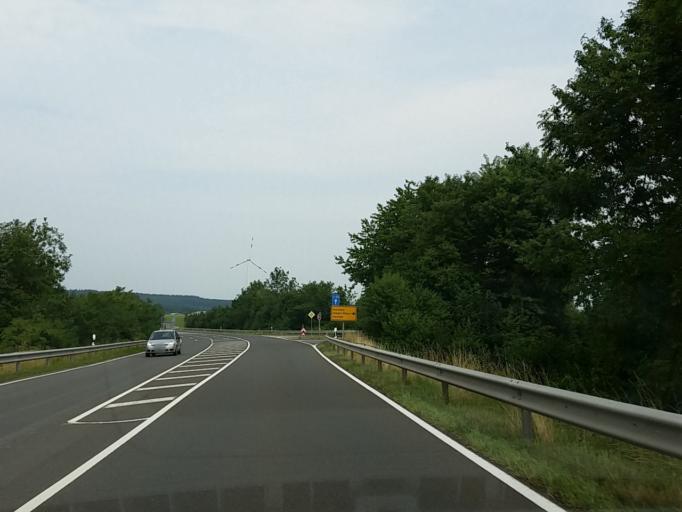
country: DE
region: Rheinland-Pfalz
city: Reinsfeld
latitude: 49.6808
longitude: 6.8965
